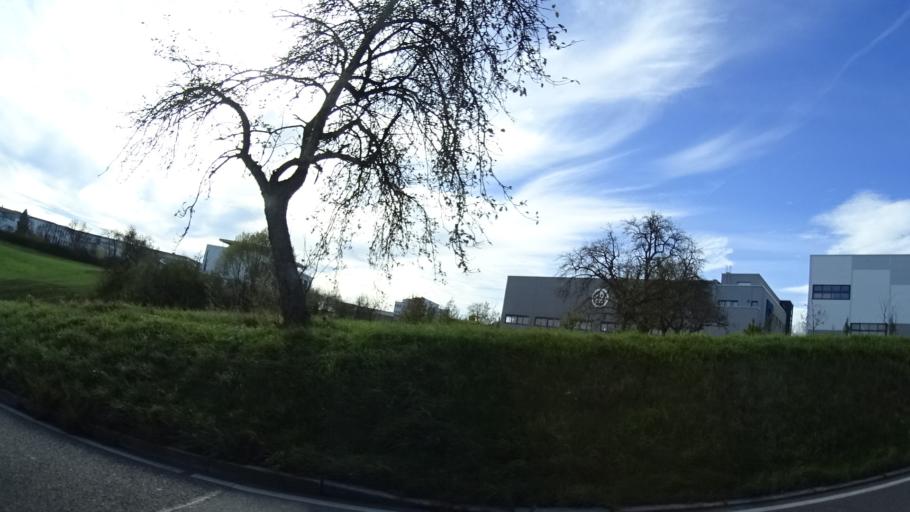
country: DE
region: Baden-Wuerttemberg
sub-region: Regierungsbezirk Stuttgart
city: Rutesheim
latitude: 48.8110
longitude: 8.9295
